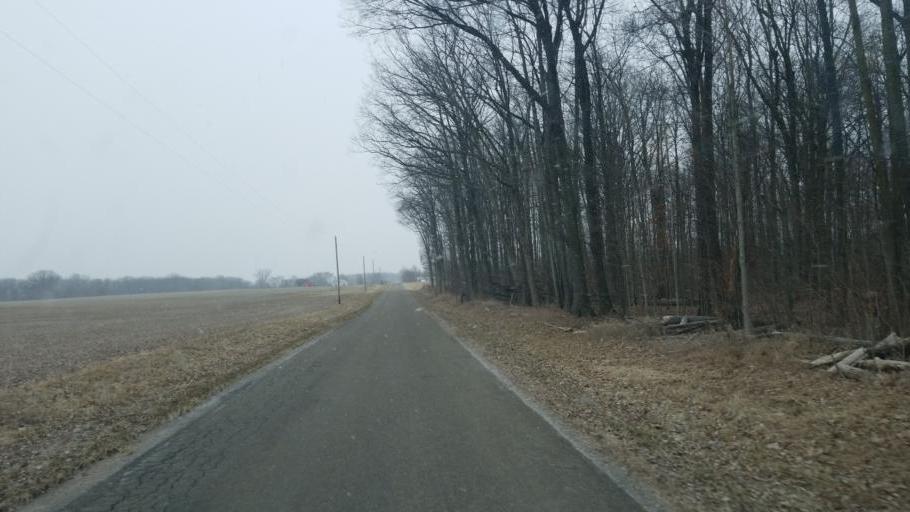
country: US
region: Ohio
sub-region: Defiance County
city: Hicksville
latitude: 41.3390
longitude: -84.7383
